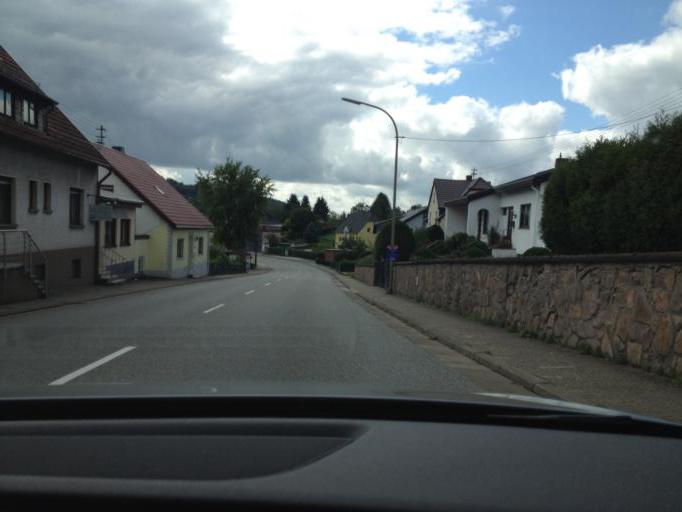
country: DE
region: Saarland
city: Namborn
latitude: 49.5306
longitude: 7.1711
